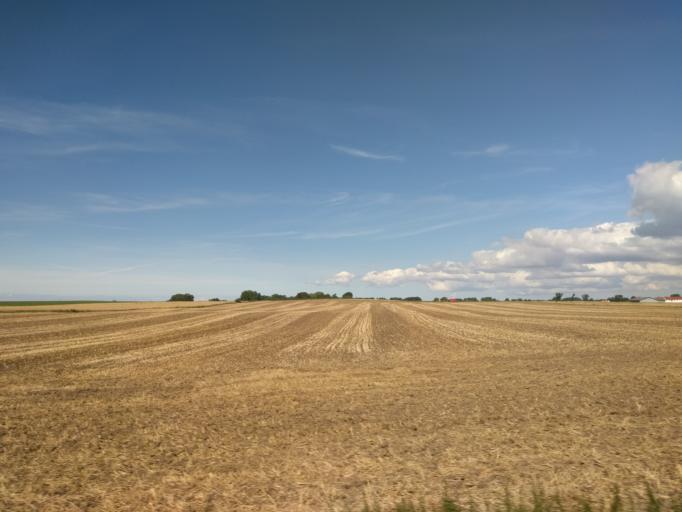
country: DK
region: Zealand
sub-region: Slagelse Kommune
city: Korsor
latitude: 55.3627
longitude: 11.1975
